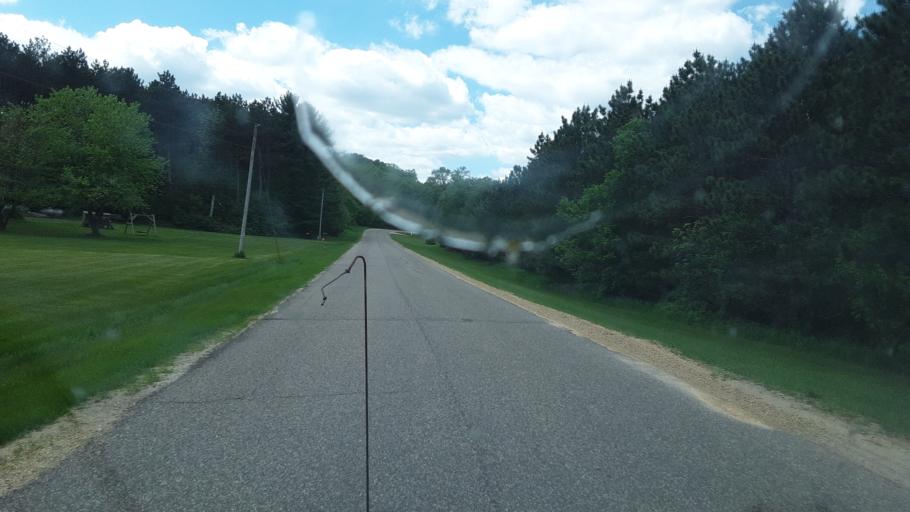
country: US
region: Wisconsin
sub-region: Sauk County
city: Reedsburg
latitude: 43.5631
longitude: -89.9924
